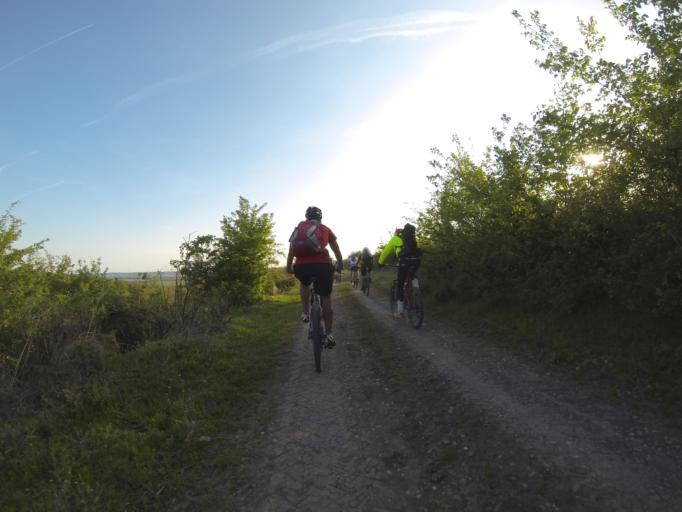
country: RO
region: Dolj
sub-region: Comuna Bradesti
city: Bradesti
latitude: 44.5290
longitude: 23.6110
